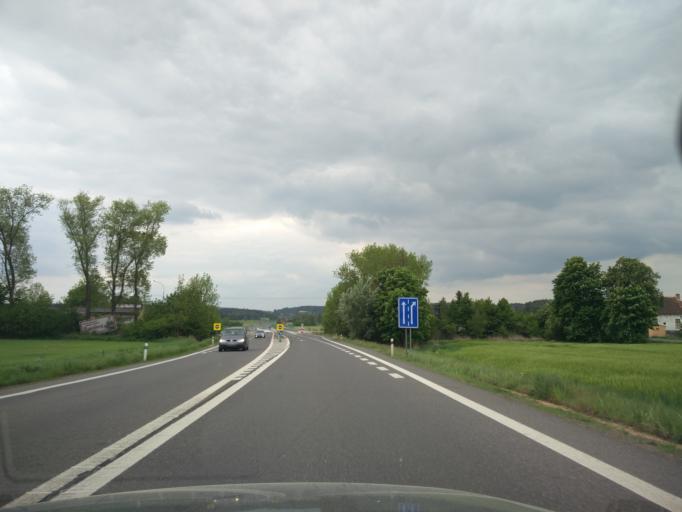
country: CZ
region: Jihocesky
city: Mirotice
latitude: 49.4148
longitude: 14.0371
